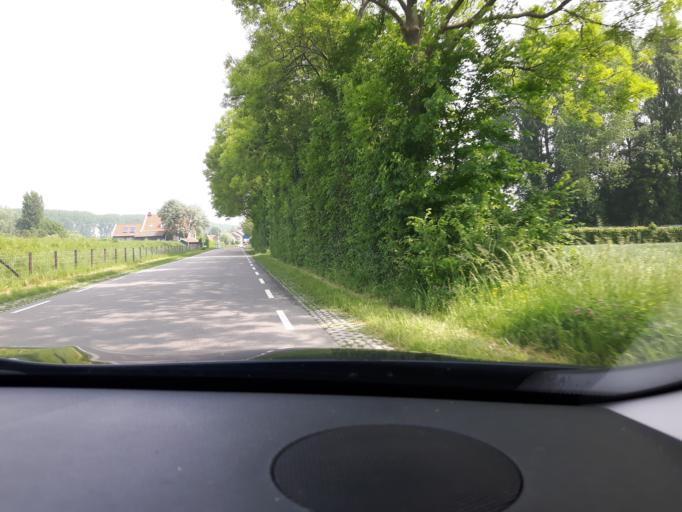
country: NL
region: Zeeland
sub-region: Gemeente Goes
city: Goes
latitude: 51.4349
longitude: 3.8838
